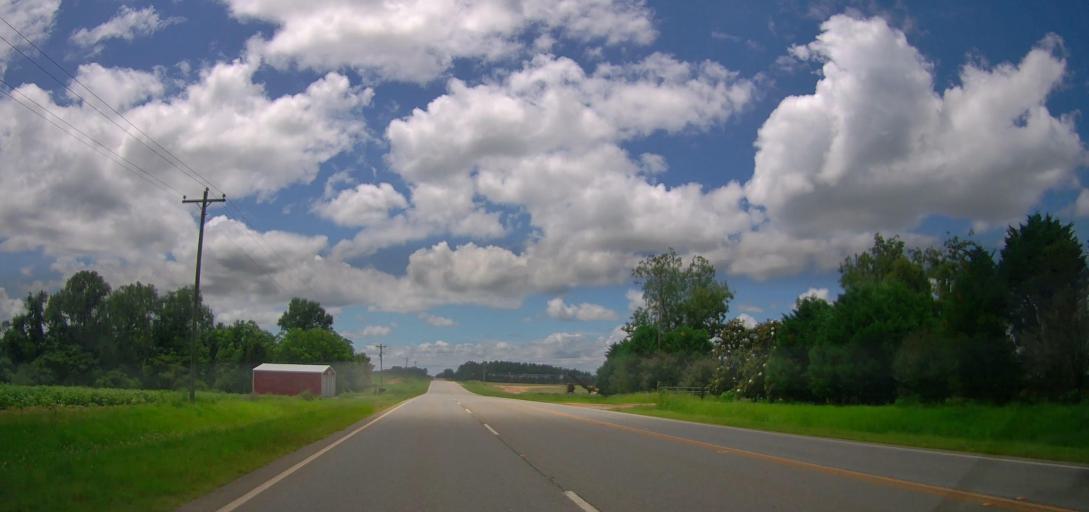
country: US
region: Georgia
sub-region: Turner County
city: Ashburn
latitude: 31.7219
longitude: -83.5275
